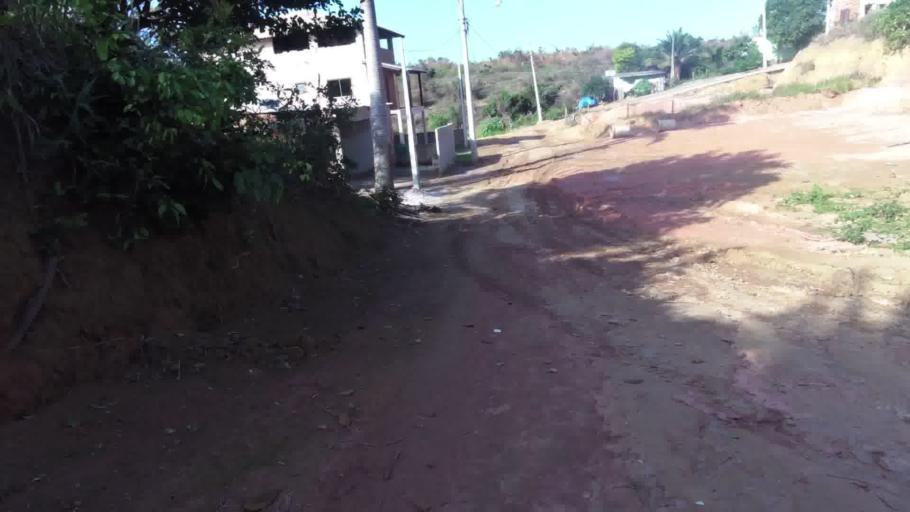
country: BR
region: Espirito Santo
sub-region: Piuma
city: Piuma
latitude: -20.8163
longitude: -40.6224
